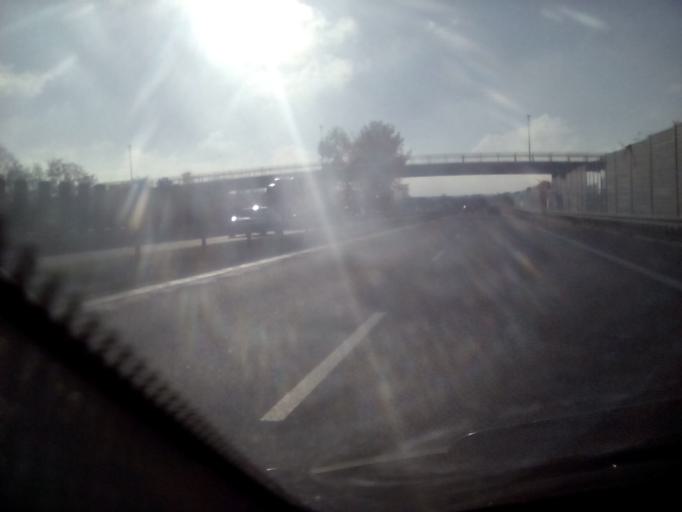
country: PL
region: Masovian Voivodeship
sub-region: Powiat grojecki
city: Grojec
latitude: 51.8464
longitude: 20.8720
